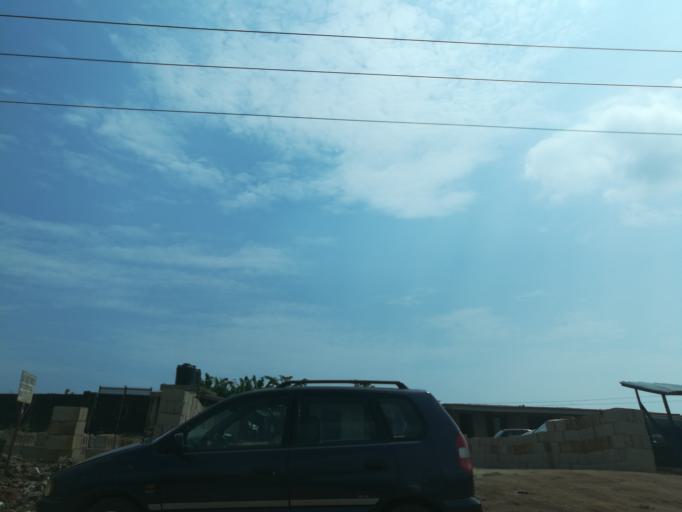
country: NG
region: Lagos
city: Ikorodu
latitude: 6.5946
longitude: 3.6359
